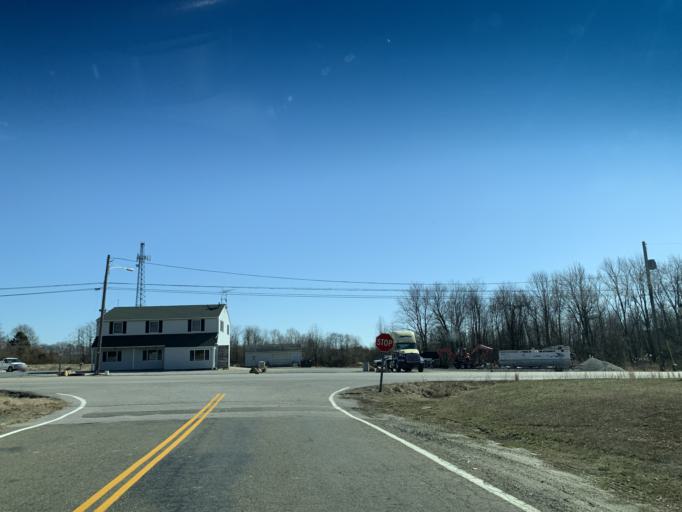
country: US
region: Maryland
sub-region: Cecil County
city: Elkton
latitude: 39.5121
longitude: -75.8276
